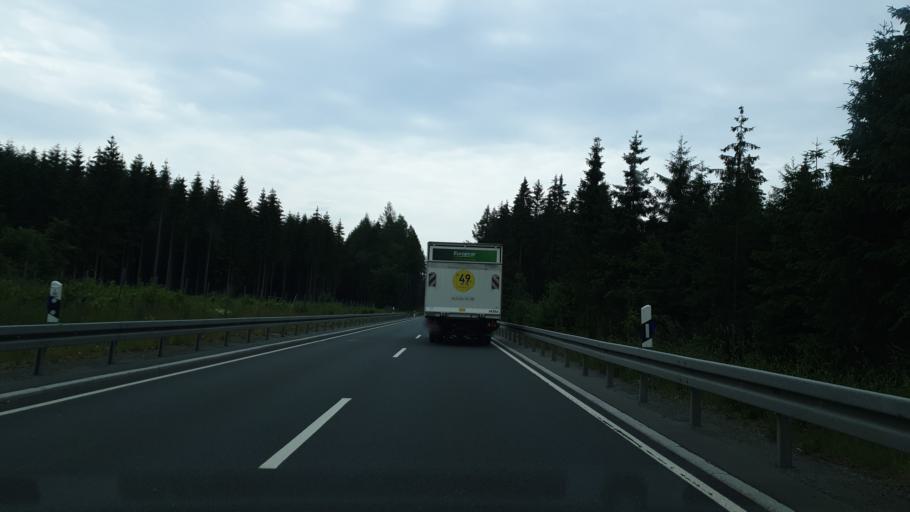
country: DE
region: Saxony
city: Tannenbergsthal
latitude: 50.4659
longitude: 12.4372
